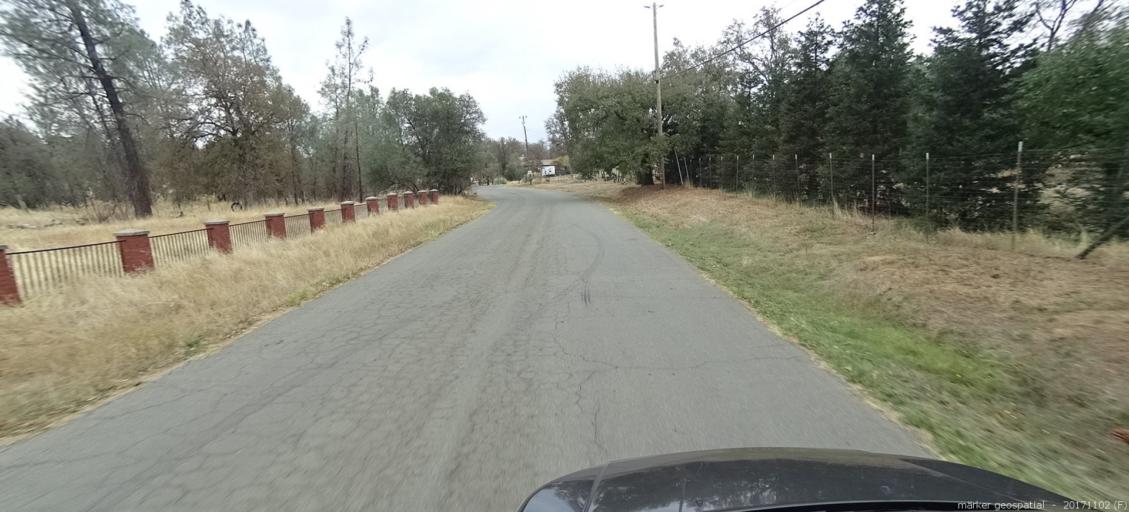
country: US
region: California
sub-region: Shasta County
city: Shasta Lake
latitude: 40.6547
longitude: -122.3140
